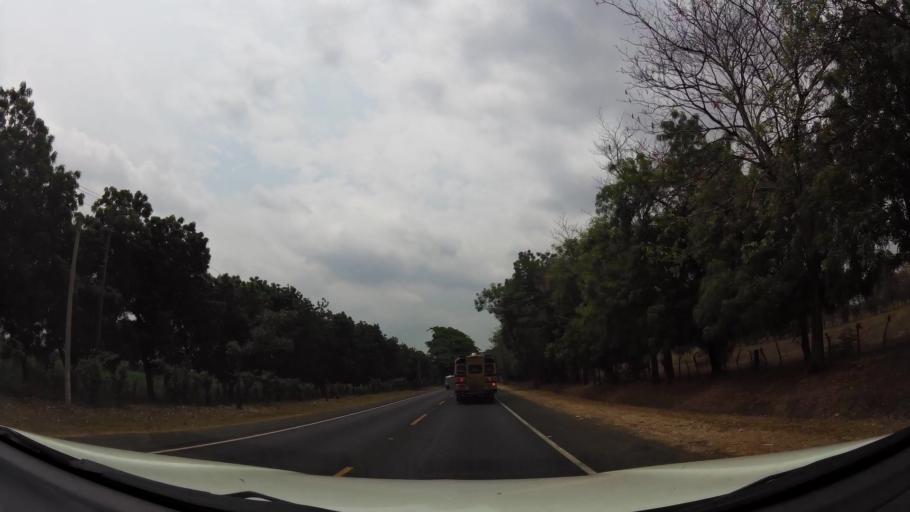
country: NI
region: Leon
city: Telica
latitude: 12.5045
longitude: -86.8602
